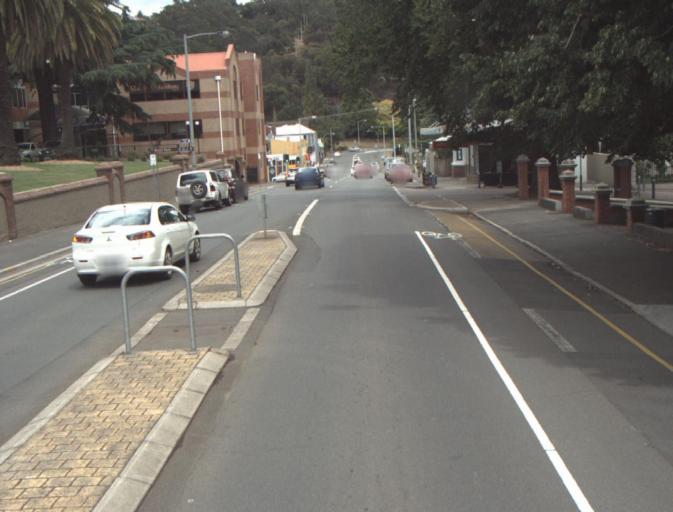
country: AU
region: Tasmania
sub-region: Launceston
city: Launceston
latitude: -41.4392
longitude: 147.1328
